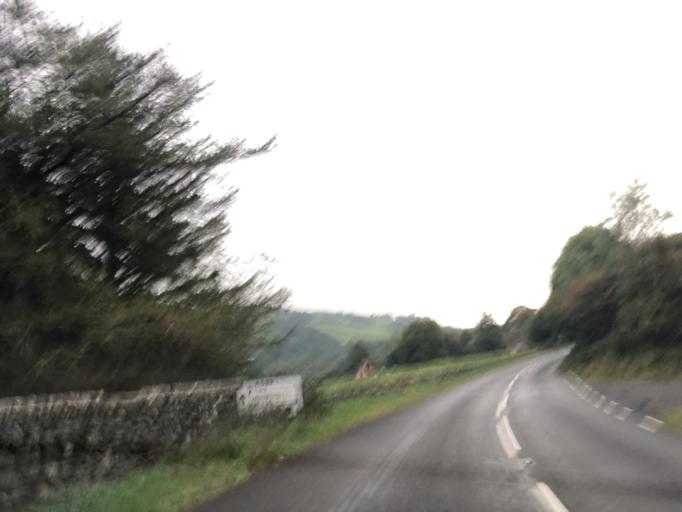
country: GB
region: England
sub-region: Cumbria
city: Windermere
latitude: 54.4288
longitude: -2.9030
